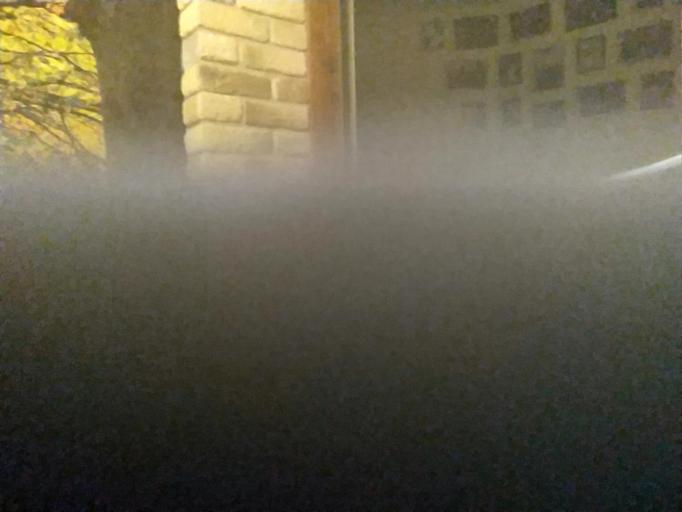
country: RU
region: Moskovskaya
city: Klin
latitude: 56.1414
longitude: 36.6727
